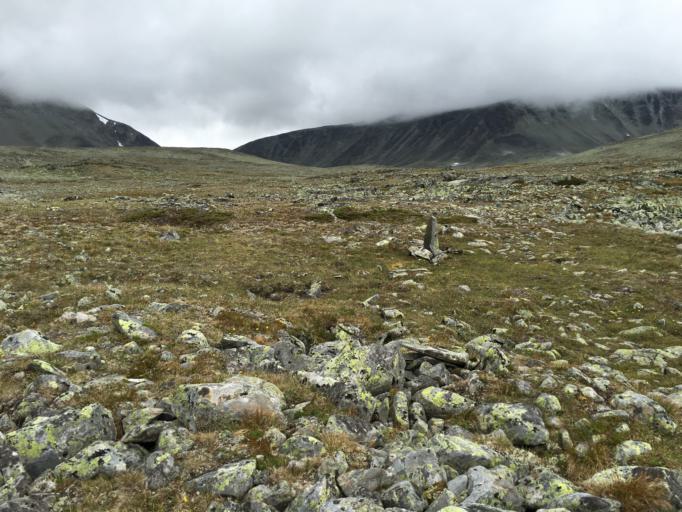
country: NO
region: Oppland
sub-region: Lom
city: Fossbergom
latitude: 61.5848
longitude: 8.7197
